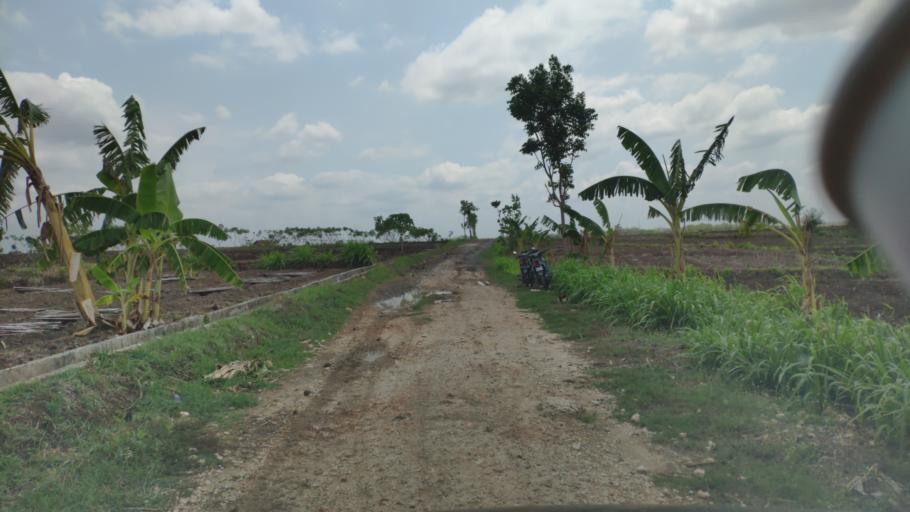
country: ID
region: Central Java
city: Gumiring
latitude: -7.0285
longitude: 111.3794
